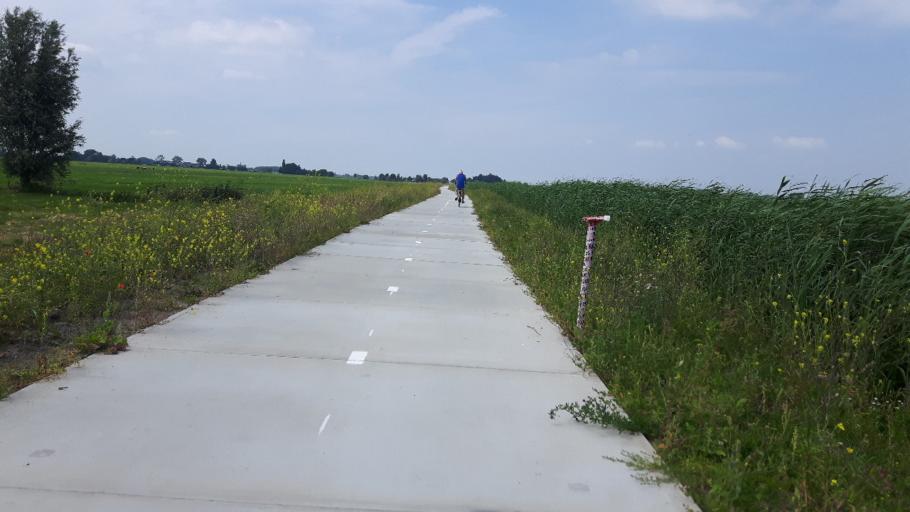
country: NL
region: South Holland
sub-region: Molenwaard
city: Liesveld
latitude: 51.8940
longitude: 4.8544
